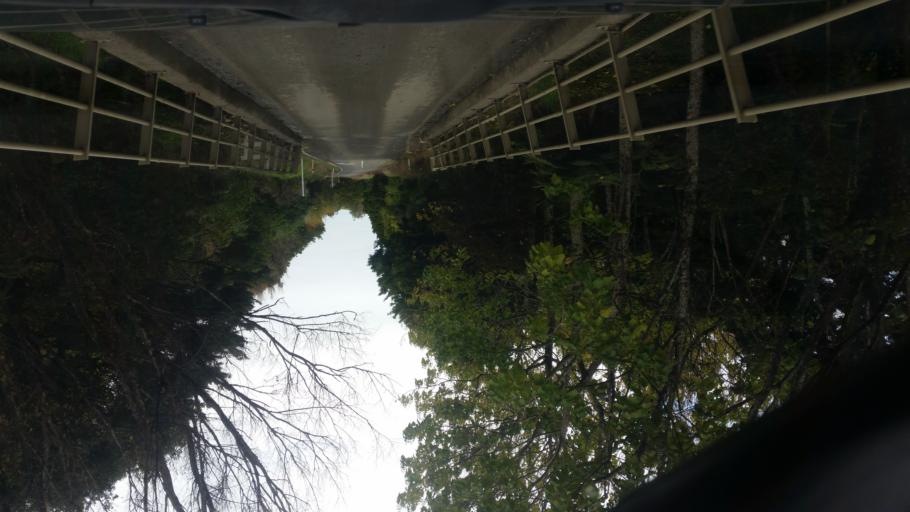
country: NZ
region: Northland
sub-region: Kaipara District
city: Dargaville
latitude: -35.7499
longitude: 173.9046
